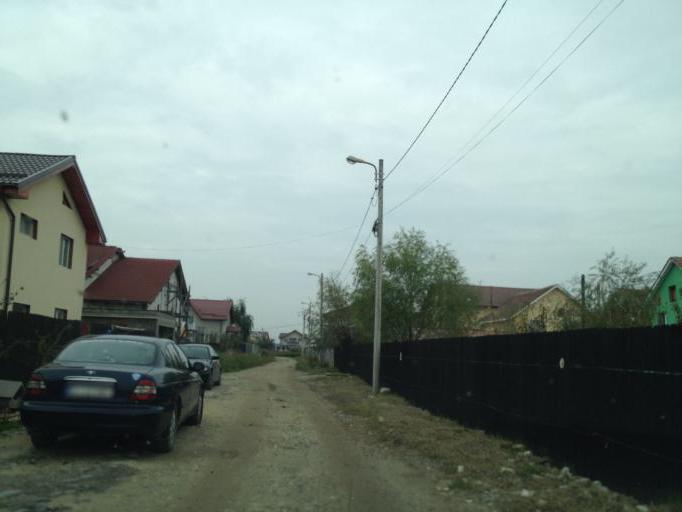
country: RO
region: Dolj
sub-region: Municipiul Craiova
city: Popoveni
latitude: 44.2925
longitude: 23.7825
